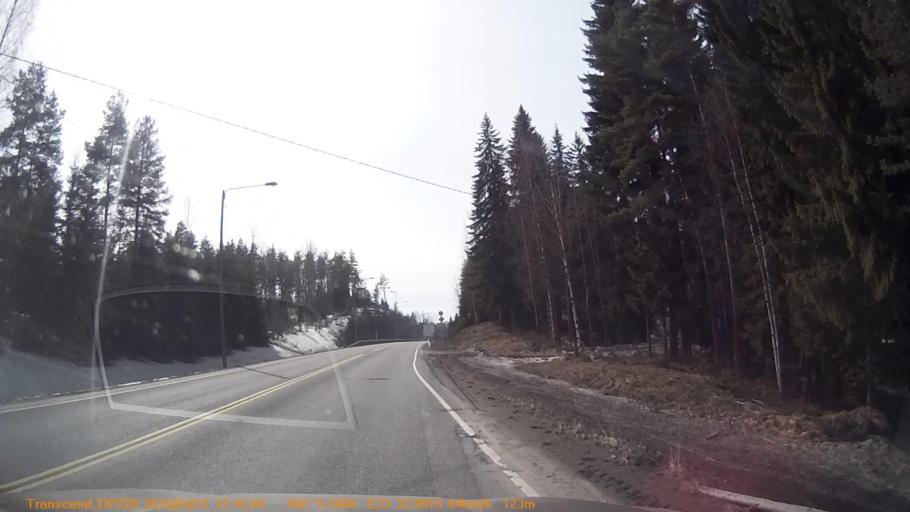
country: FI
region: Pirkanmaa
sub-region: Etelae-Pirkanmaa
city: Urjala
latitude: 61.0859
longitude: 23.5496
